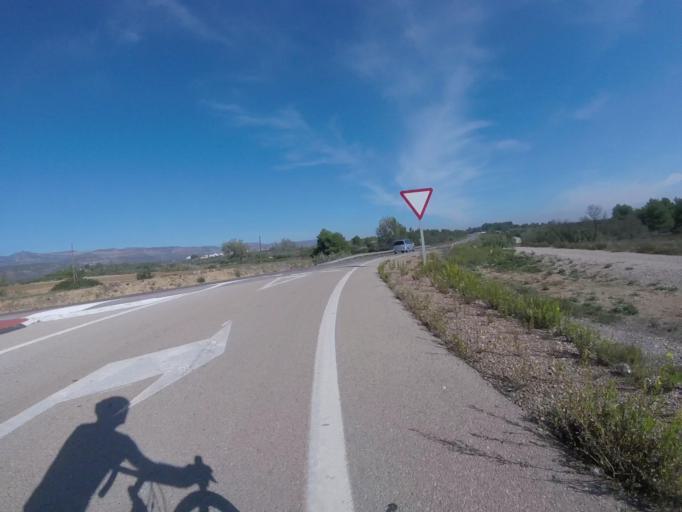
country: ES
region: Valencia
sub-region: Provincia de Castello
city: Benlloch
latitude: 40.2531
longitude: 0.0749
